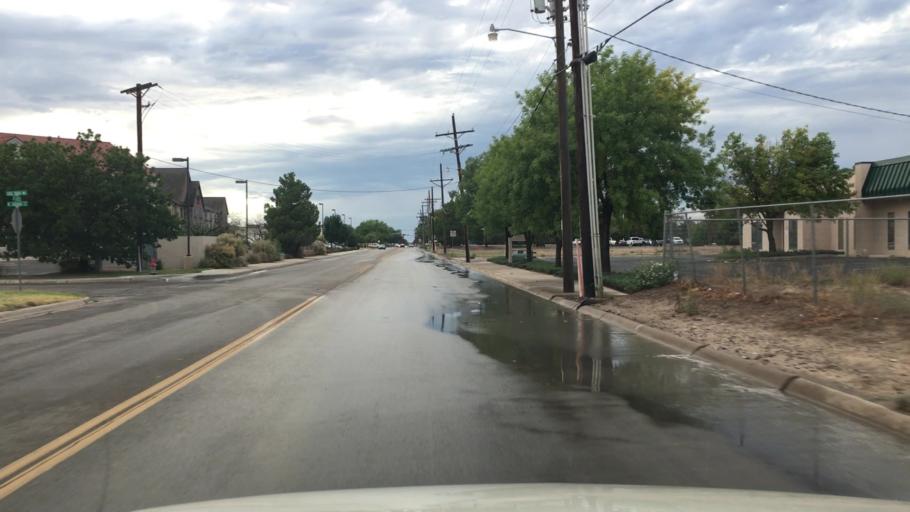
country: US
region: New Mexico
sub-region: Chaves County
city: Roswell
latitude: 33.4160
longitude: -104.5186
